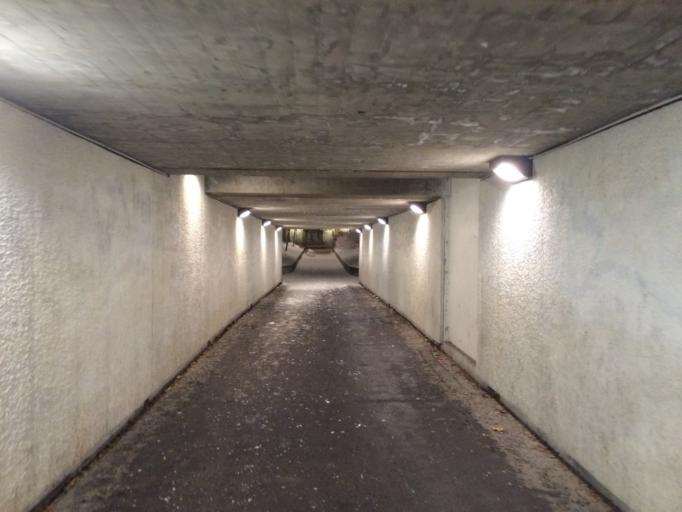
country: SE
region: Vaesterbotten
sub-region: Skelleftea Kommun
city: Skelleftea
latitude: 64.7538
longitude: 20.9534
